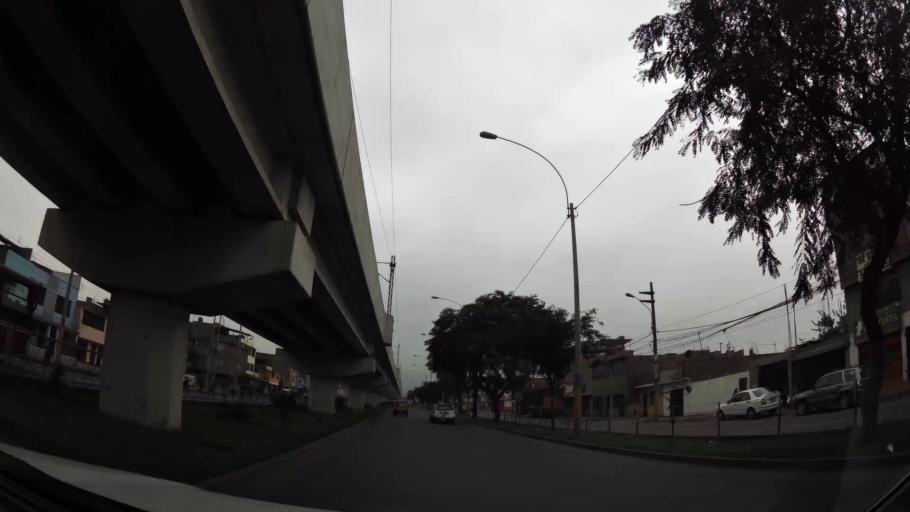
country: PE
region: Lima
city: Lima
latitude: -12.0246
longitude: -77.0090
